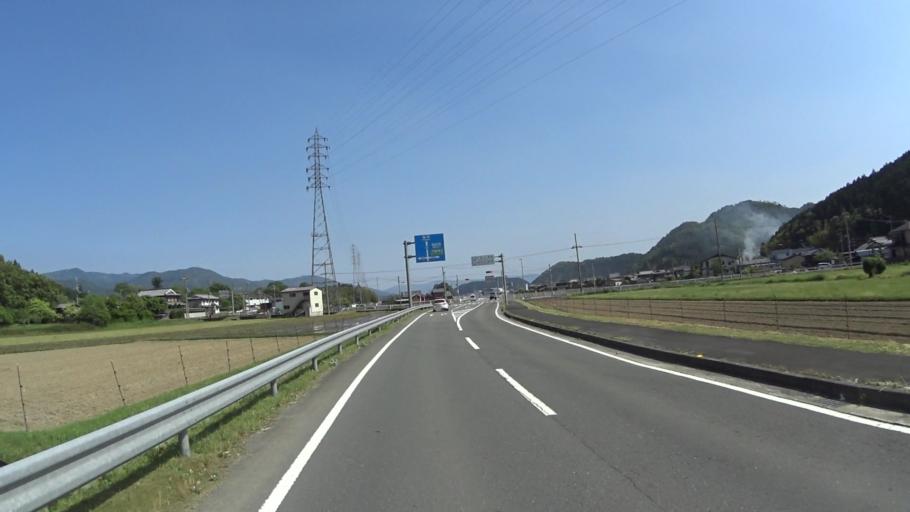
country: JP
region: Kyoto
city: Kameoka
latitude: 35.1053
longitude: 135.5262
